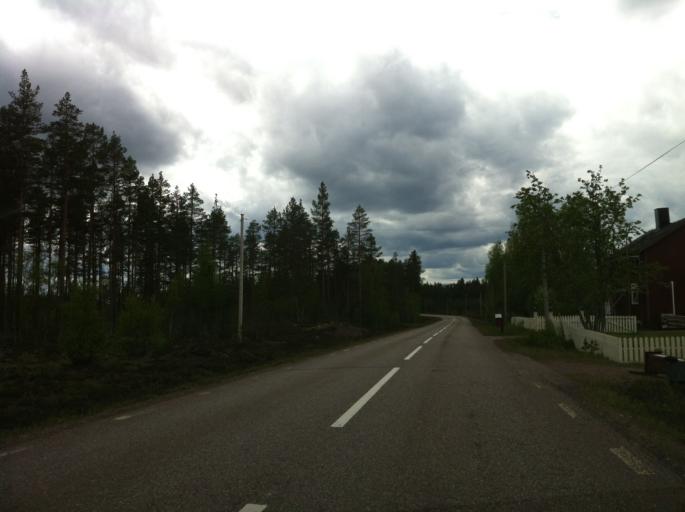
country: NO
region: Hedmark
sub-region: Trysil
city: Innbygda
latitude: 61.4316
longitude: 13.0958
